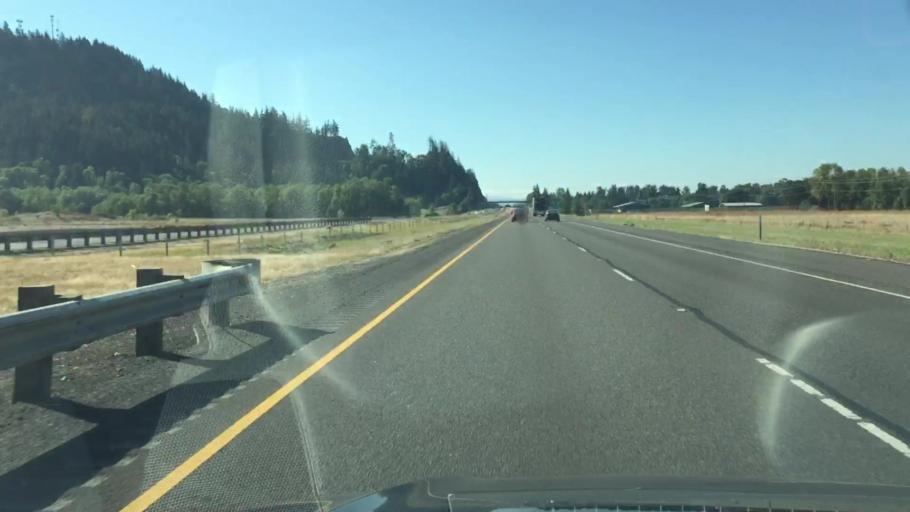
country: US
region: Oregon
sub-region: Lane County
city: Coburg
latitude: 44.1261
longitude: -123.0493
